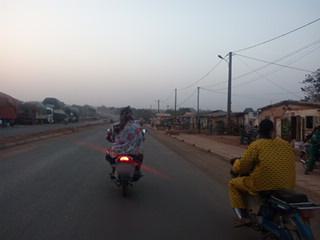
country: BJ
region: Borgou
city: Parakou
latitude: 9.3422
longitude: 2.6029
